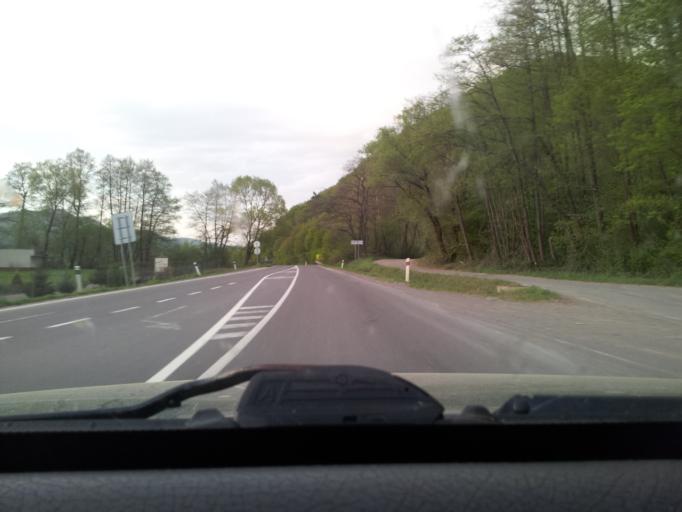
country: SK
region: Banskobystricky
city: Zarnovica
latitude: 48.5166
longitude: 18.7398
